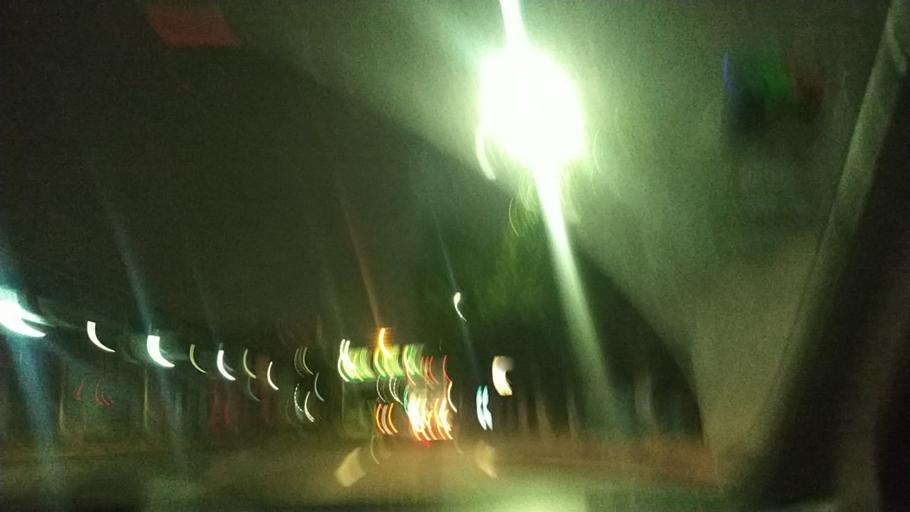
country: MX
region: Mexico
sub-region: Tultitlan
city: Fuentes del Valle
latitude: 19.6303
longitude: -99.1277
